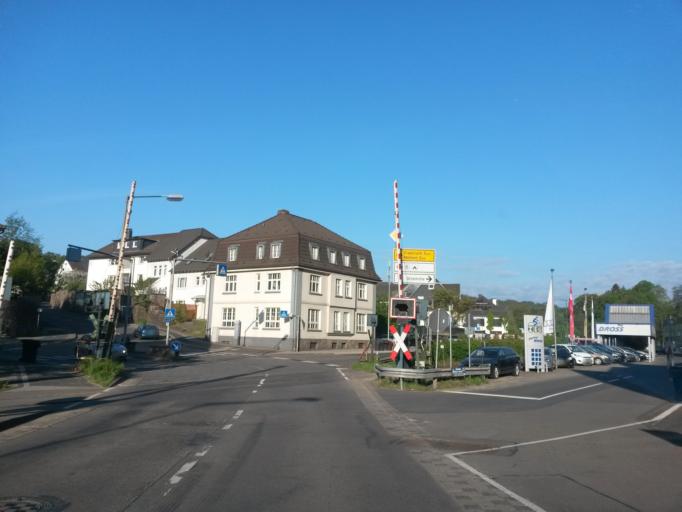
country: DE
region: North Rhine-Westphalia
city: Wiehl
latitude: 50.9634
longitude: 7.5064
